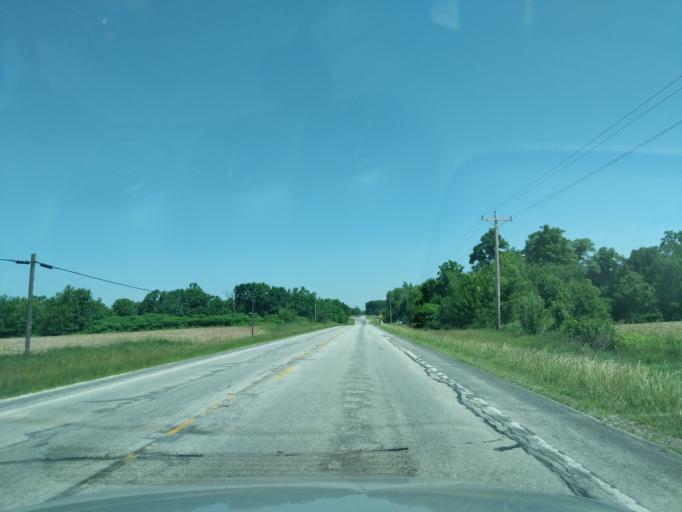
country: US
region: Indiana
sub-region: Whitley County
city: Columbia City
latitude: 41.1099
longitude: -85.4715
